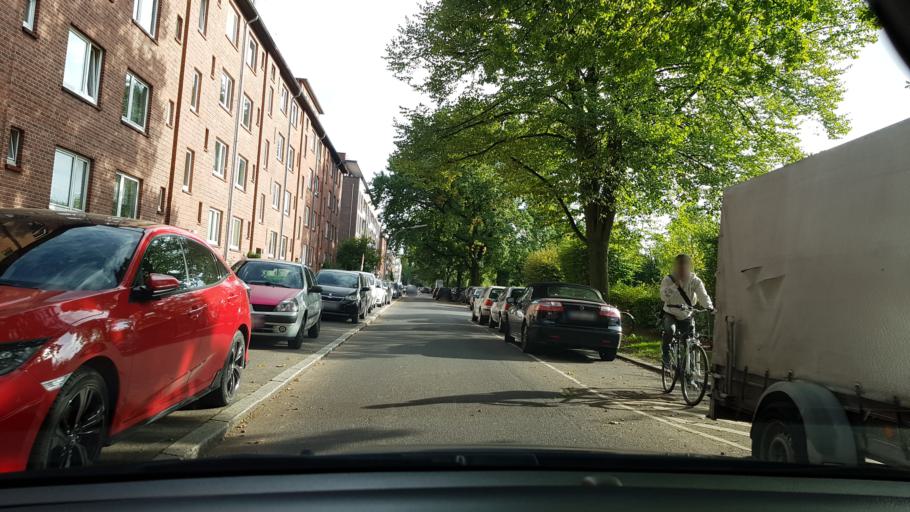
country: DE
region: Hamburg
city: Steilshoop
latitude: 53.5983
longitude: 10.0541
